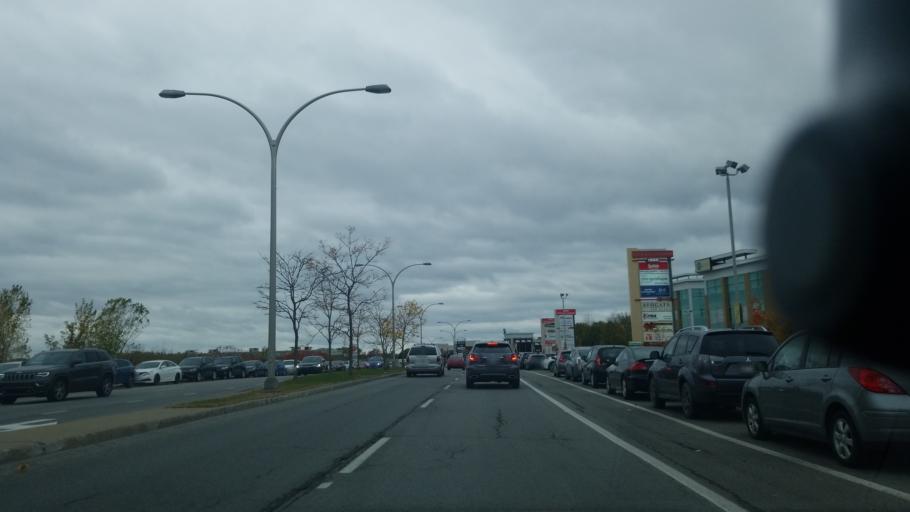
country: CA
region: Quebec
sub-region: Laval
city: Laval
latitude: 45.5645
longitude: -73.7245
